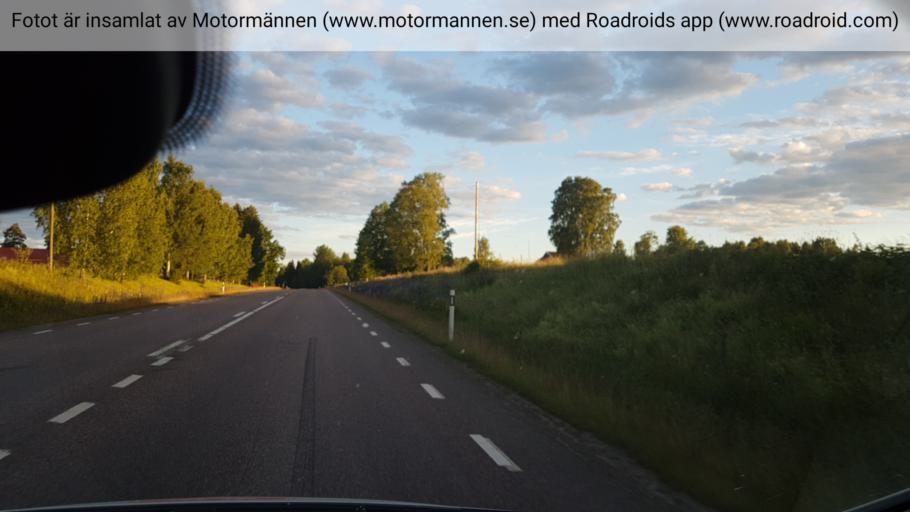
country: SE
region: Vaermland
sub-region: Sunne Kommun
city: Sunne
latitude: 59.8626
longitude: 13.1301
